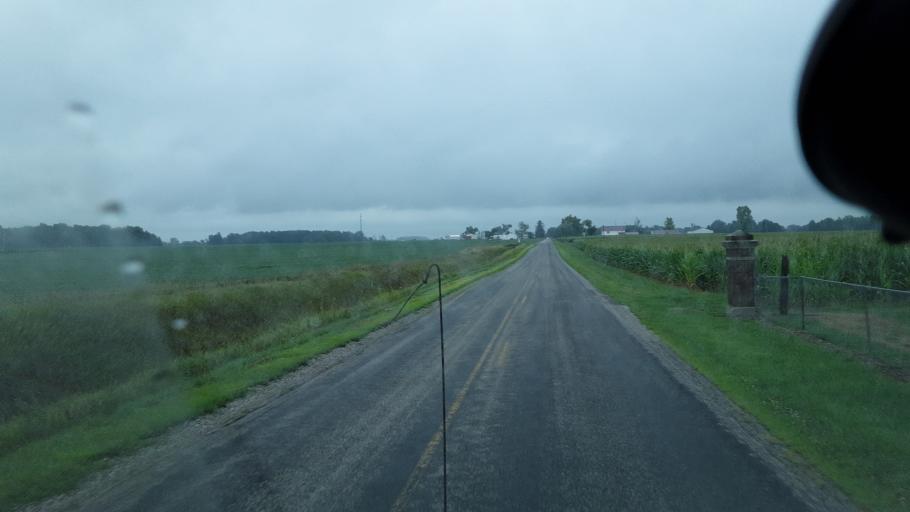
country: US
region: Indiana
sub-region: Wells County
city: Ossian
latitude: 40.8472
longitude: -85.1091
